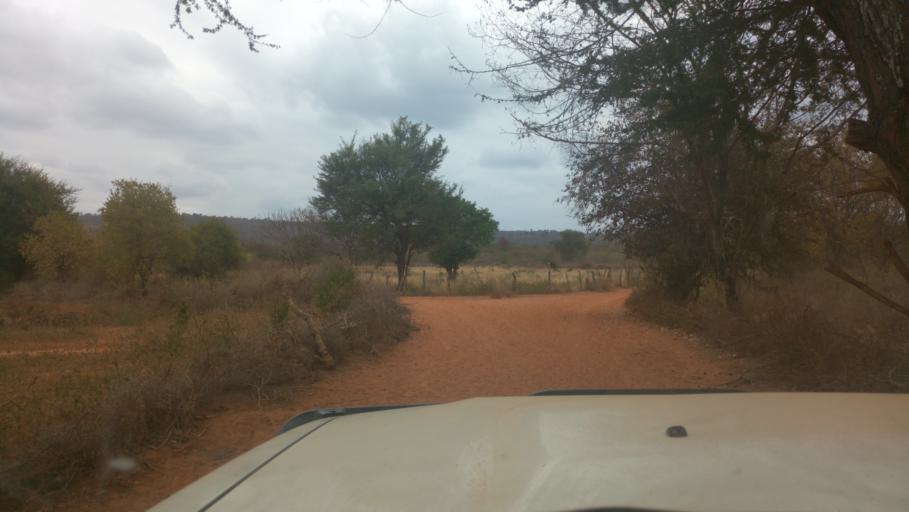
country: KE
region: Makueni
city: Wote
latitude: -1.6375
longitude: 37.8680
